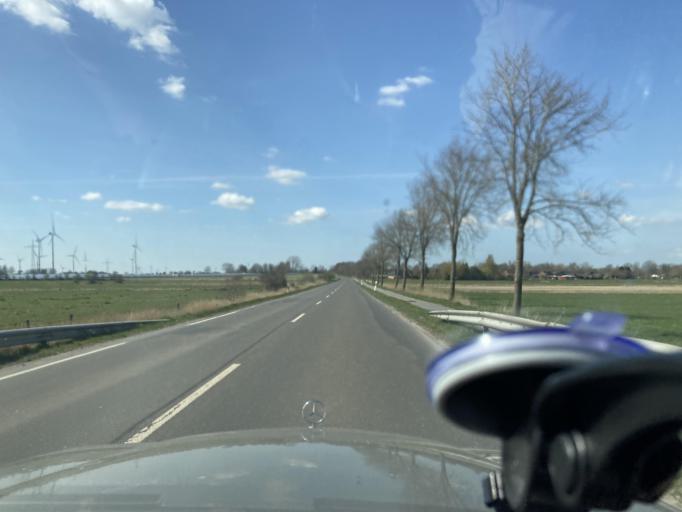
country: DE
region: Schleswig-Holstein
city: Stelle-Wittenwurth
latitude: 54.2477
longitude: 9.0709
